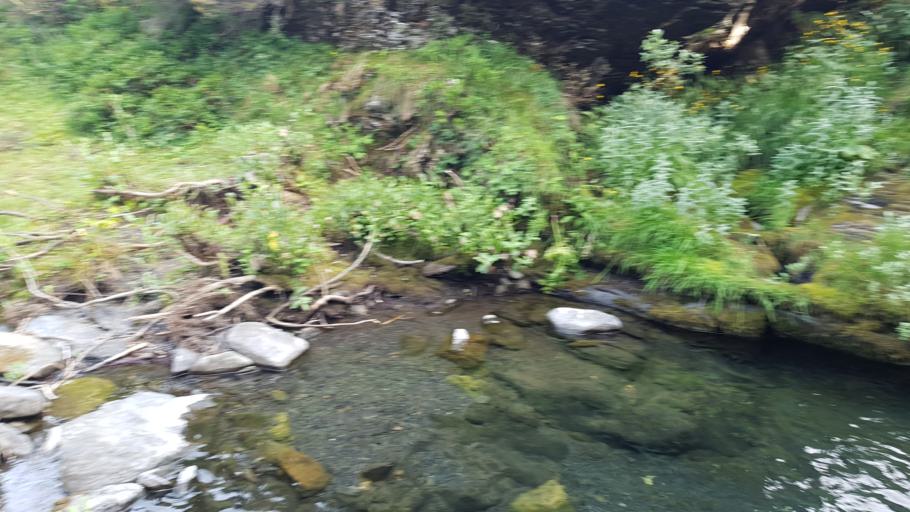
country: ES
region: Asturias
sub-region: Province of Asturias
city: Rio Aller
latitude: 43.0123
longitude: -5.4686
